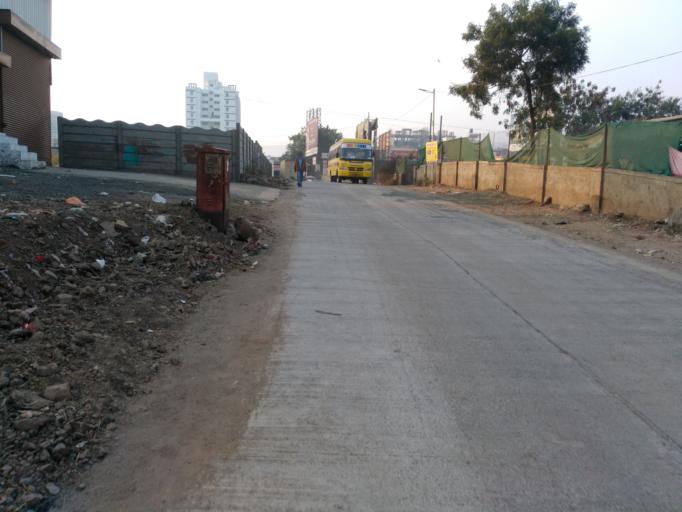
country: IN
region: Maharashtra
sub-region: Pune Division
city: Pune
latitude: 18.4507
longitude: 73.9109
